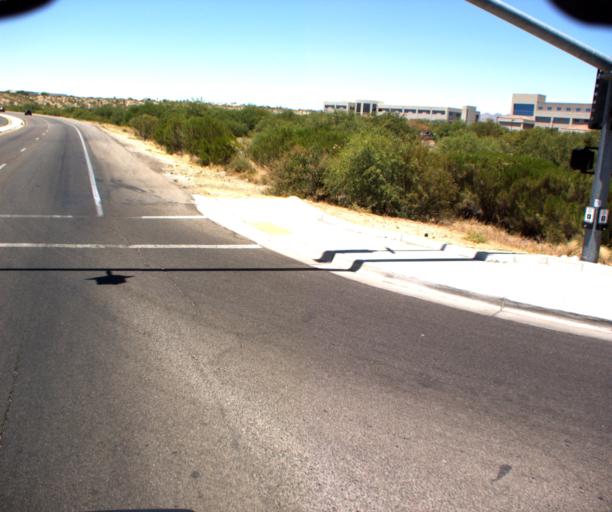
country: US
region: Arizona
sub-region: Pima County
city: Oro Valley
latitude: 32.4273
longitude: -110.9470
